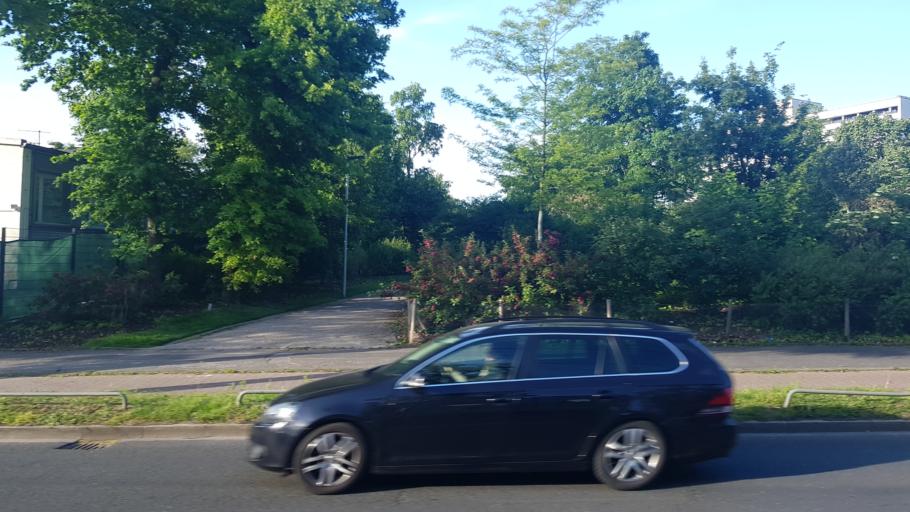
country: DE
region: North Rhine-Westphalia
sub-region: Regierungsbezirk Dusseldorf
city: Dusseldorf
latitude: 51.2331
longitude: 6.7297
